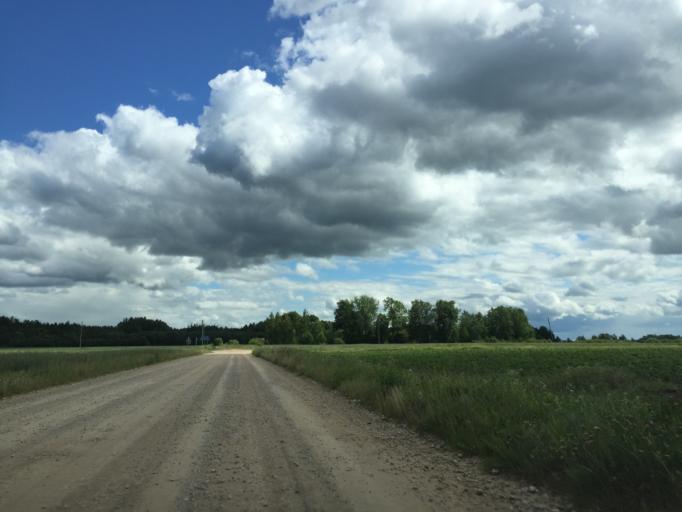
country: LV
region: Lecava
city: Iecava
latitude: 56.5008
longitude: 24.3597
